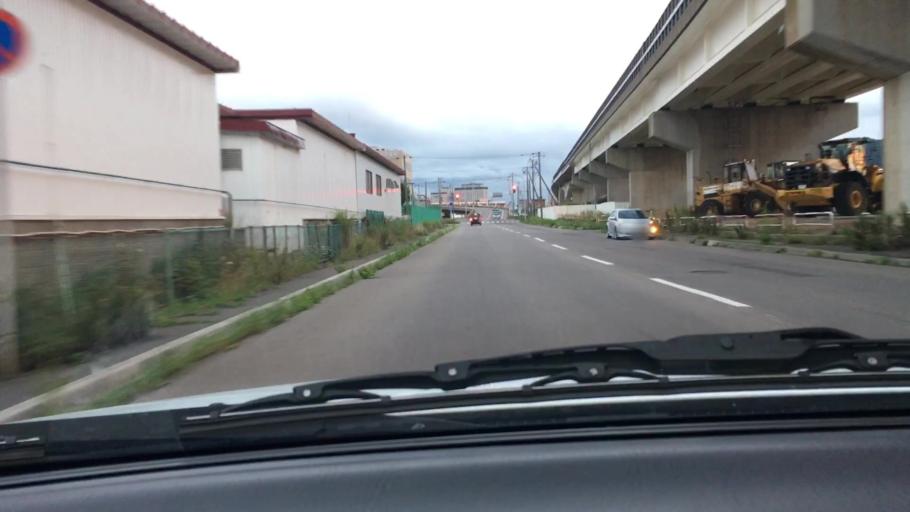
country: JP
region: Hokkaido
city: Hakodate
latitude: 41.7845
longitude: 140.7271
